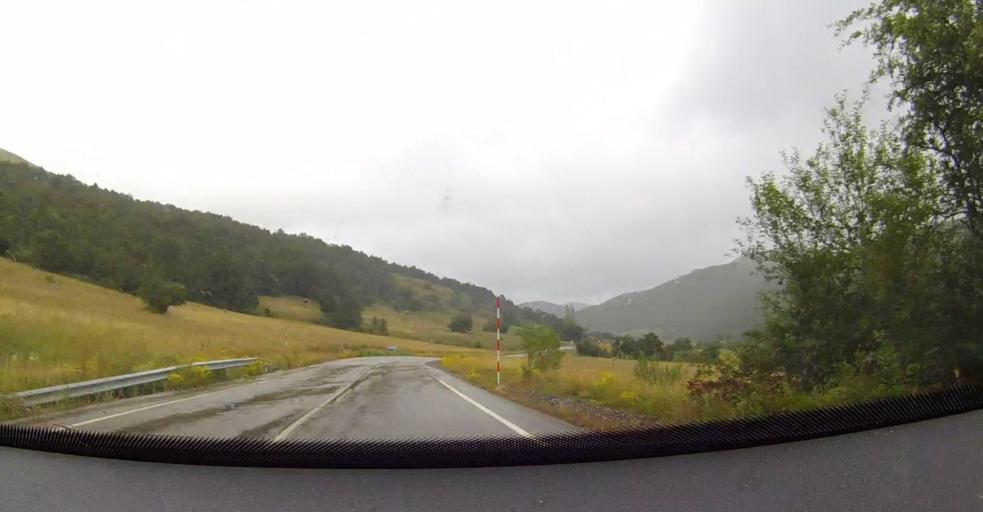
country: ES
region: Castille and Leon
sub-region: Provincia de Leon
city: Marana
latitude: 43.0703
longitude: -5.1863
